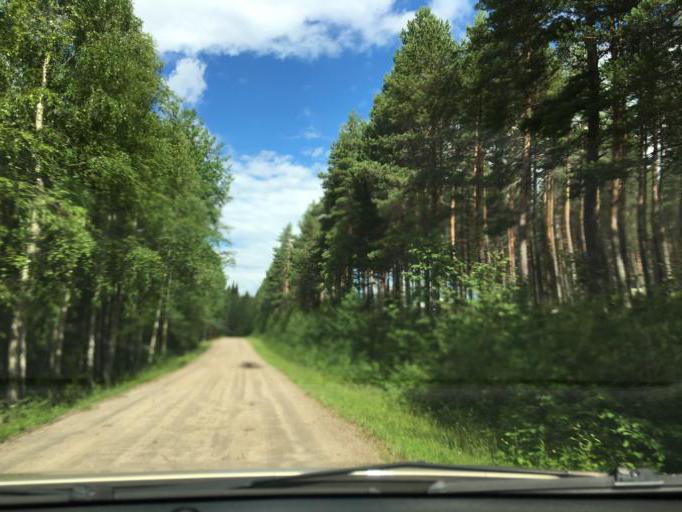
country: SE
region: Norrbotten
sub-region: Overkalix Kommun
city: OEverkalix
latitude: 66.1297
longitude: 22.7847
